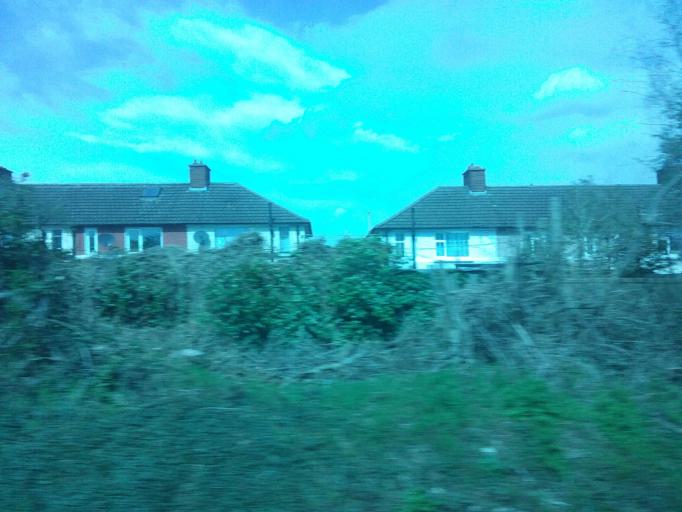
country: IE
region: Leinster
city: Chapelizod
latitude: 53.3385
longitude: -6.3405
